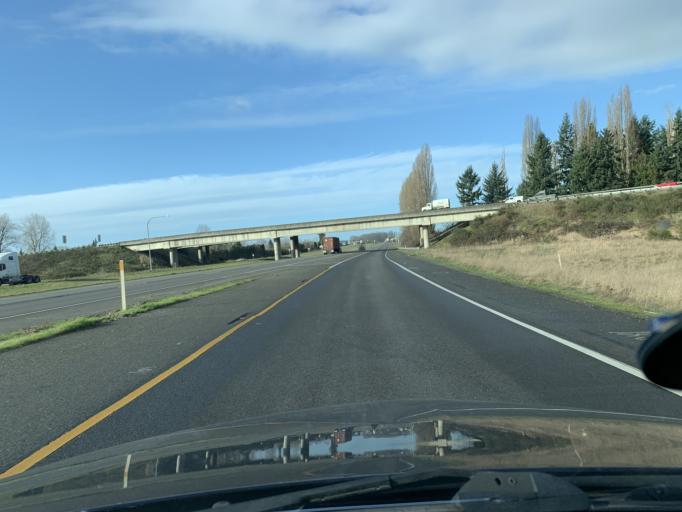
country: US
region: Washington
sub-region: Pierce County
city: North Puyallup
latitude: 47.2025
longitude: -122.2768
